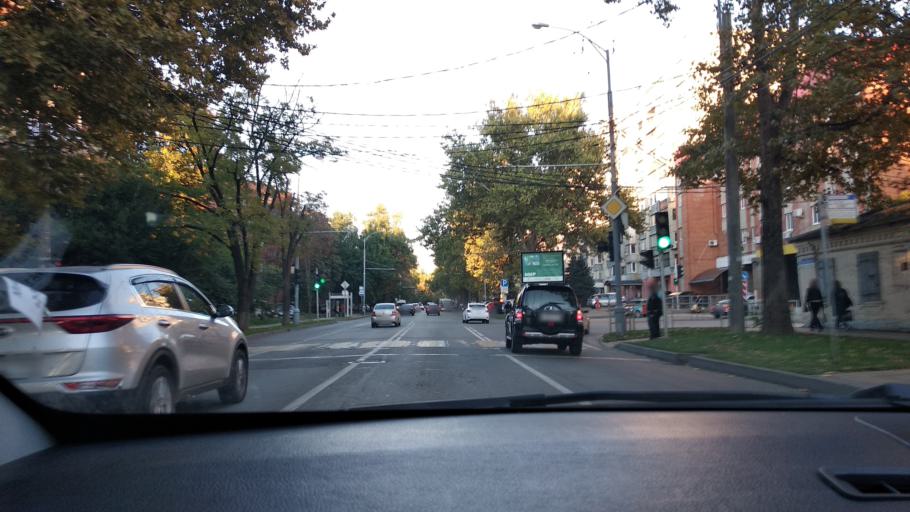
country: RU
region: Krasnodarskiy
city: Krasnodar
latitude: 45.0179
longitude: 38.9933
